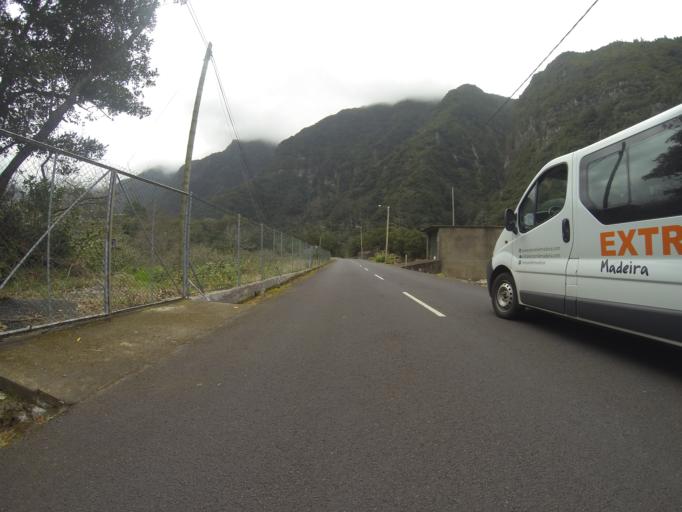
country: PT
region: Madeira
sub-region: Porto Moniz
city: Porto Moniz
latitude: 32.8112
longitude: -17.1132
